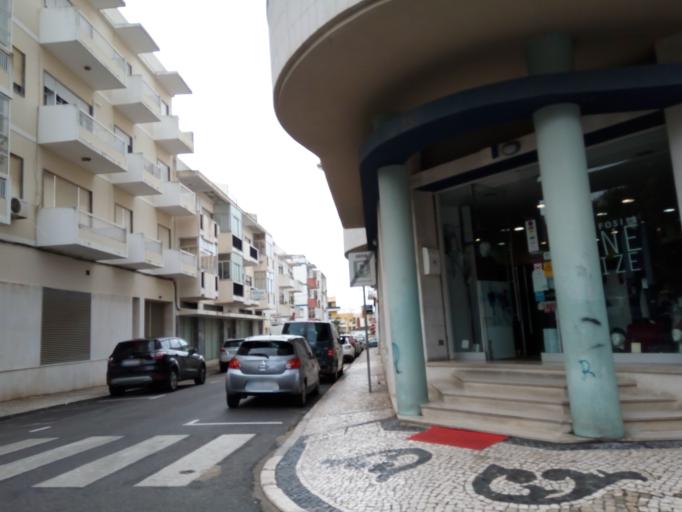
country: PT
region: Faro
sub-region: Loule
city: Loule
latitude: 37.1376
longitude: -8.0195
